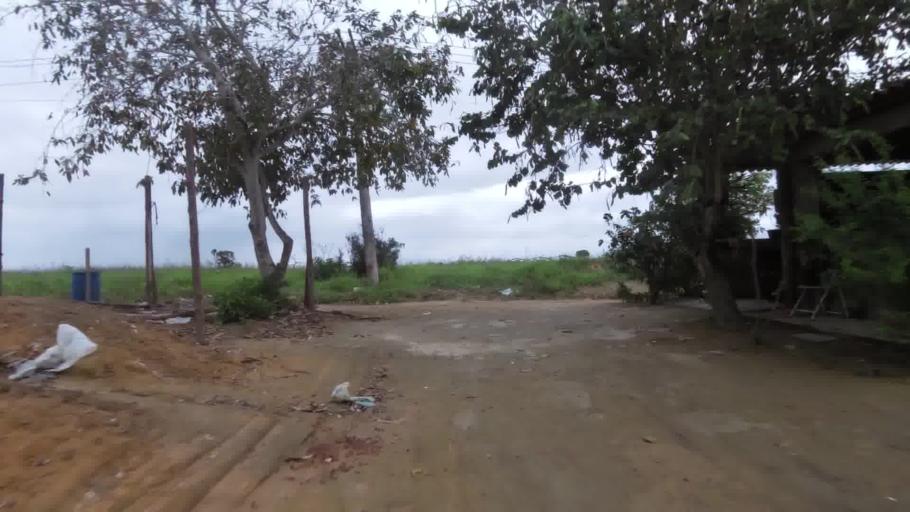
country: BR
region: Espirito Santo
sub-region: Marataizes
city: Marataizes
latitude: -21.0408
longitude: -40.8363
